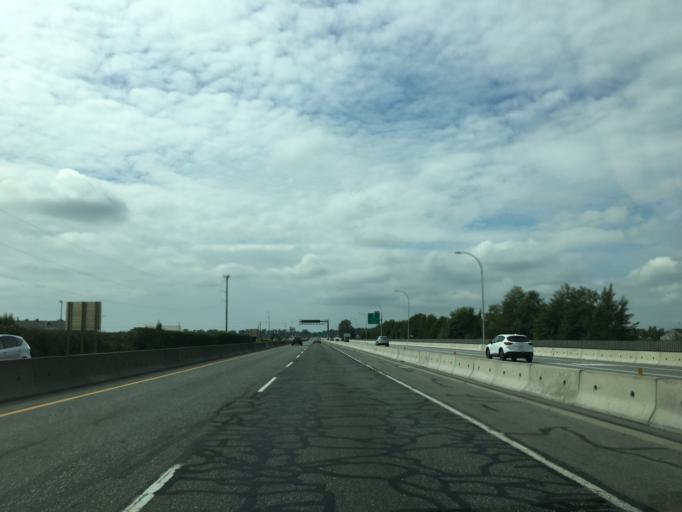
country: CA
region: British Columbia
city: Ladner
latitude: 49.1013
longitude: -123.0411
